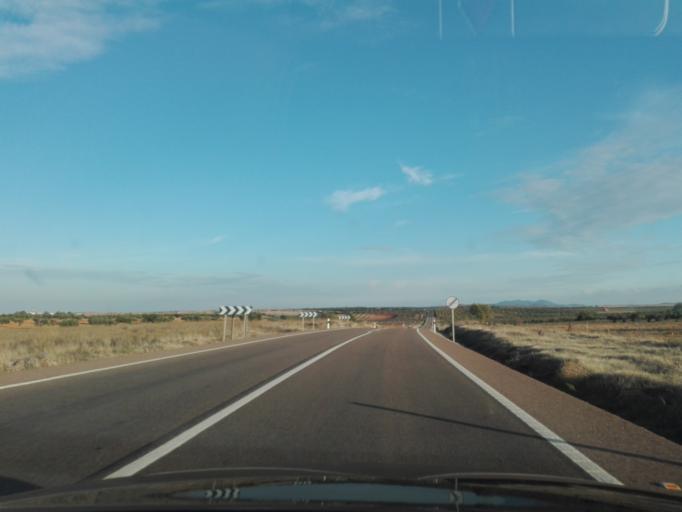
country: ES
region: Extremadura
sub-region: Provincia de Badajoz
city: Usagre
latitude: 38.3512
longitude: -6.1939
